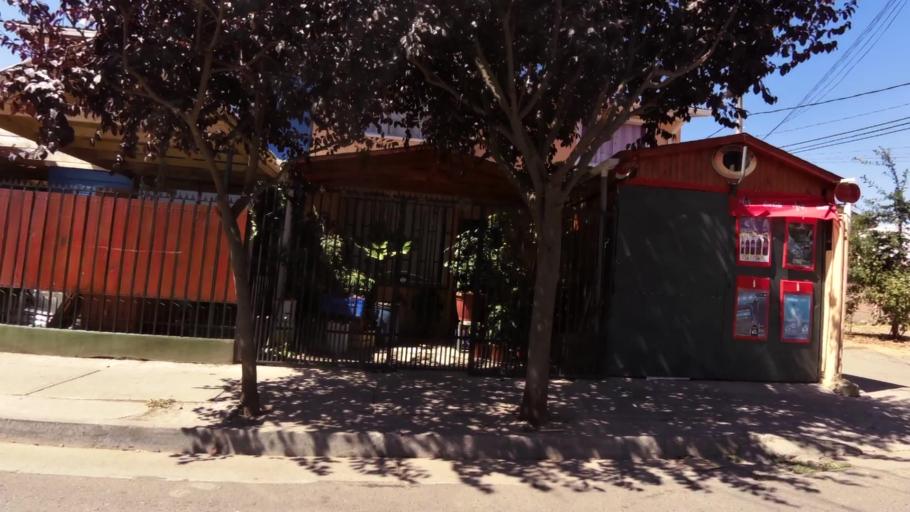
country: CL
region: O'Higgins
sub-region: Provincia de Colchagua
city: Chimbarongo
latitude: -34.5647
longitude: -70.9957
